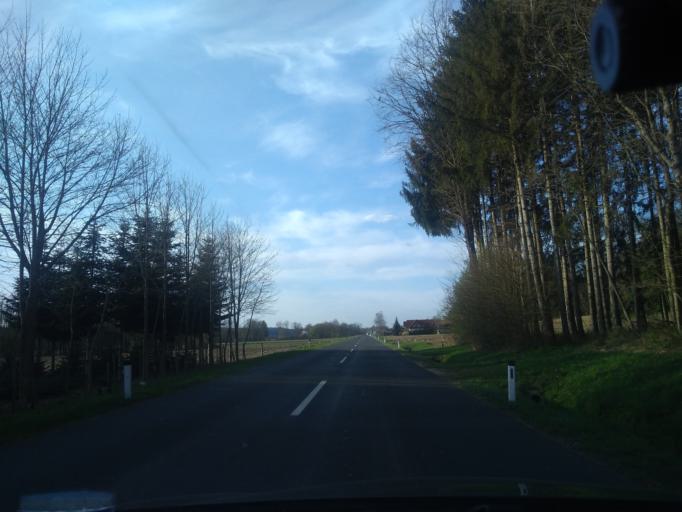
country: AT
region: Styria
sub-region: Politischer Bezirk Suedoststeiermark
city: Gosdorf
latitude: 46.7418
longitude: 15.7789
